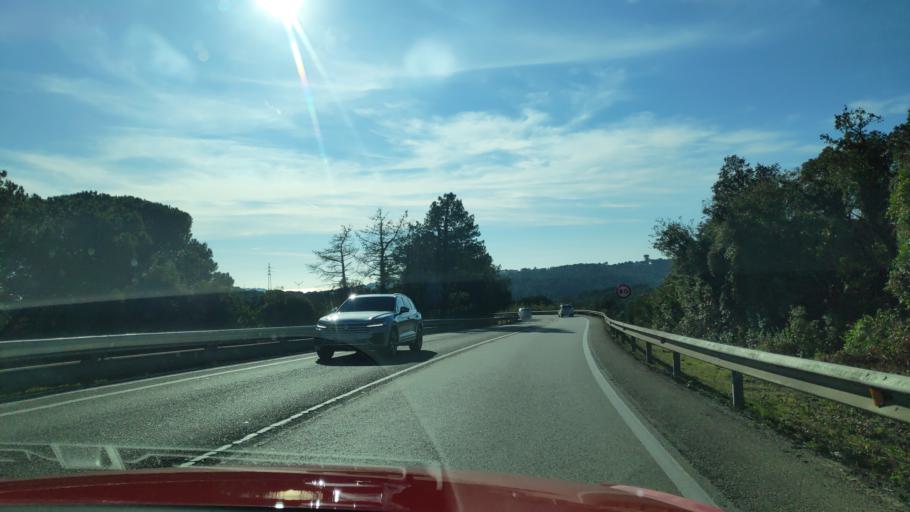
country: ES
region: Catalonia
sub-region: Provincia de Girona
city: Lloret de Mar
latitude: 41.7223
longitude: 2.8252
